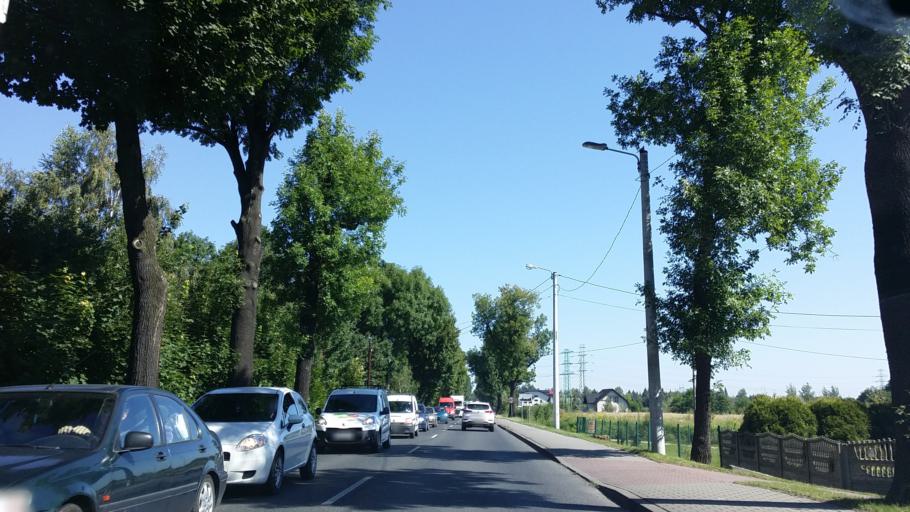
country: PL
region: Lesser Poland Voivodeship
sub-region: Powiat oswiecimski
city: Babice
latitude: 50.0803
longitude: 19.1948
